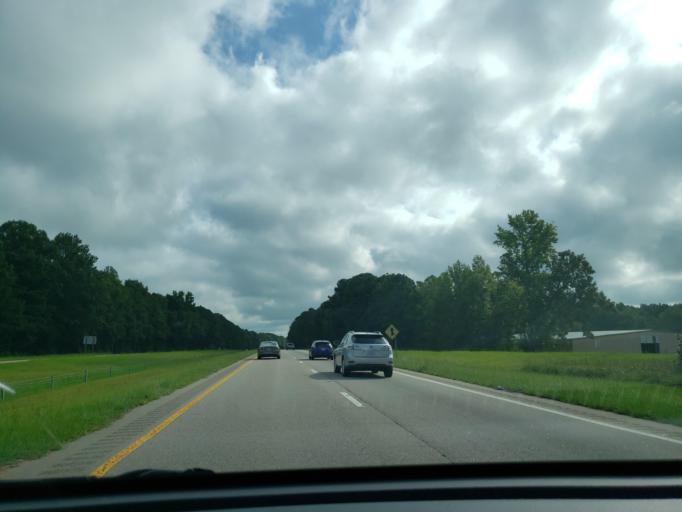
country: US
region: North Carolina
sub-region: Wake County
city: Zebulon
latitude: 35.8797
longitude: -78.2210
